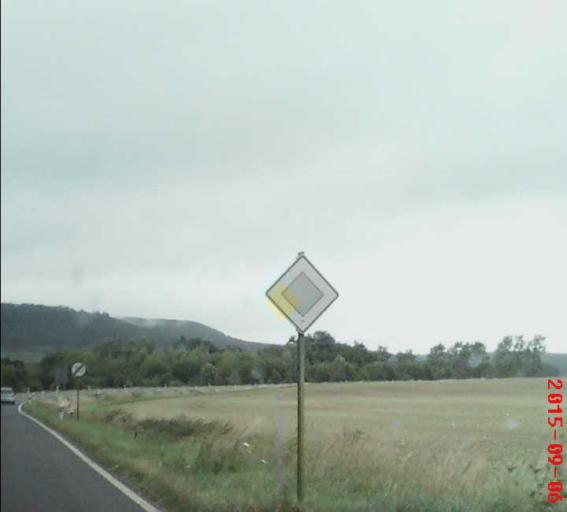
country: DE
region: Thuringia
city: Breitenworbis
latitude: 51.4027
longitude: 10.4341
